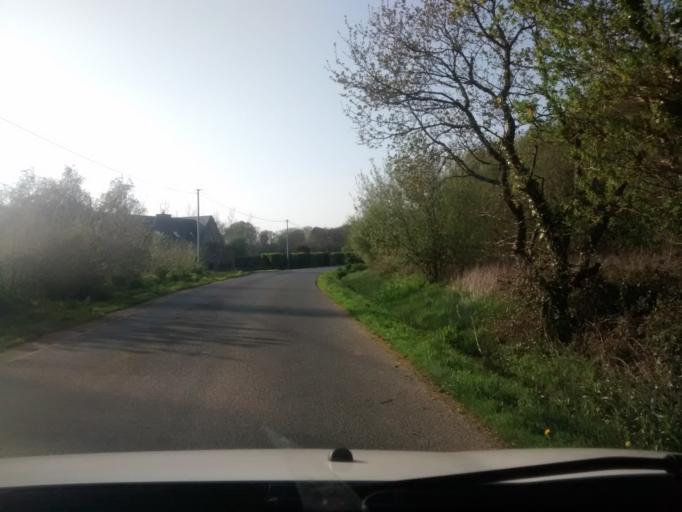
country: FR
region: Brittany
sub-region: Departement des Cotes-d'Armor
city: Trevou-Treguignec
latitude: 48.8010
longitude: -3.3501
